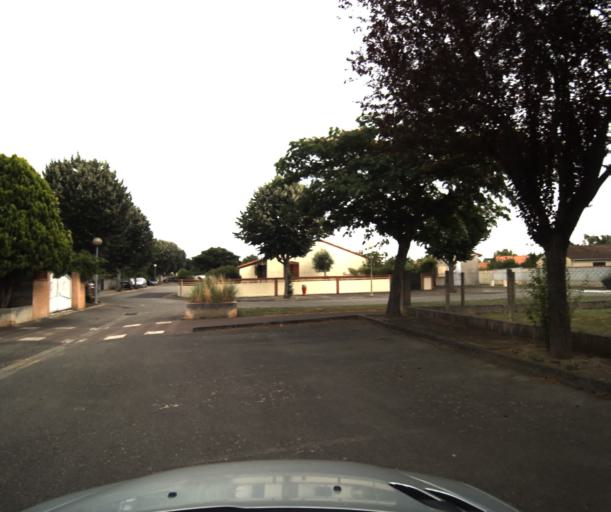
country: FR
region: Midi-Pyrenees
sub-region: Departement de la Haute-Garonne
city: Portet-sur-Garonne
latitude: 43.5371
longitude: 1.4081
